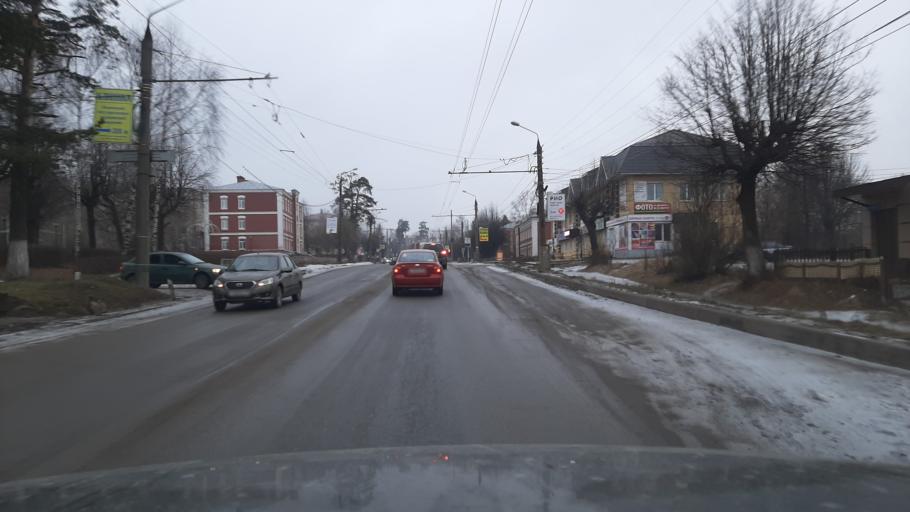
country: RU
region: Ivanovo
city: Kokhma
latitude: 56.9318
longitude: 41.0790
